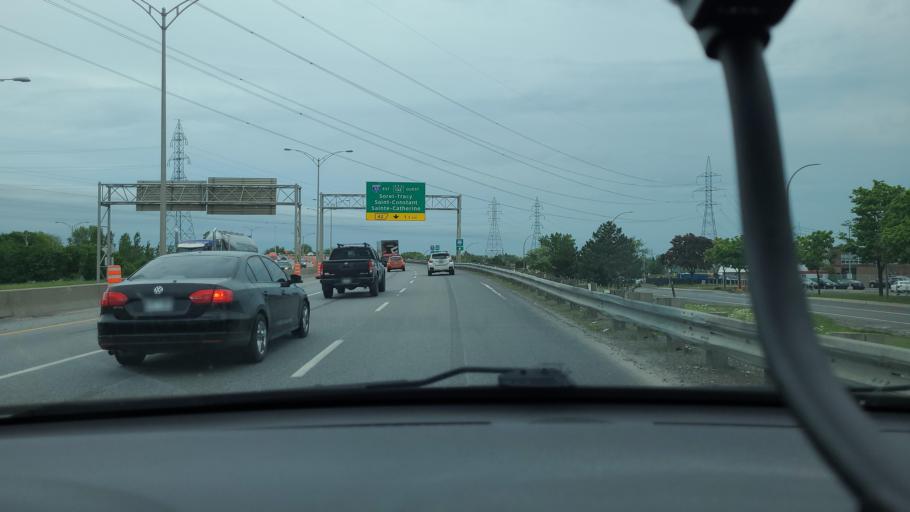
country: CA
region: Quebec
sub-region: Monteregie
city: Candiac
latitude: 45.3931
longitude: -73.5133
